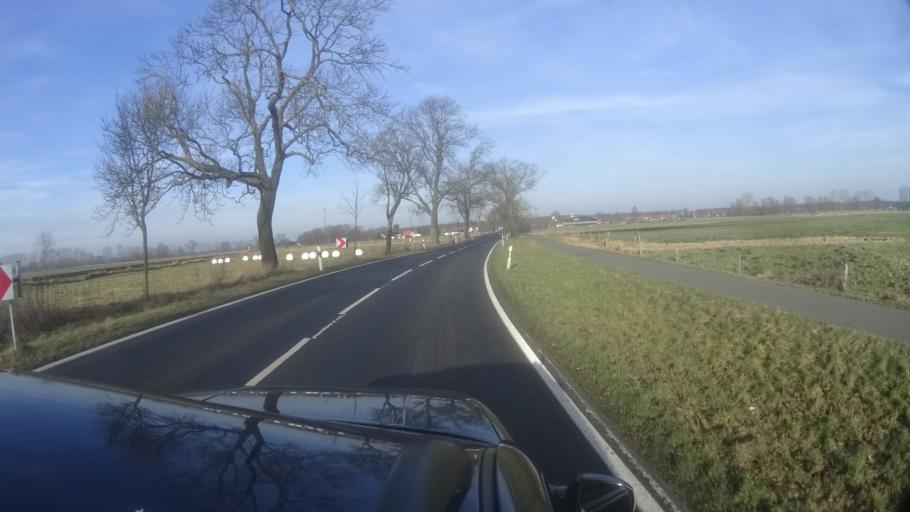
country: DE
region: Brandenburg
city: Kremmen
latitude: 52.7945
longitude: 13.0362
